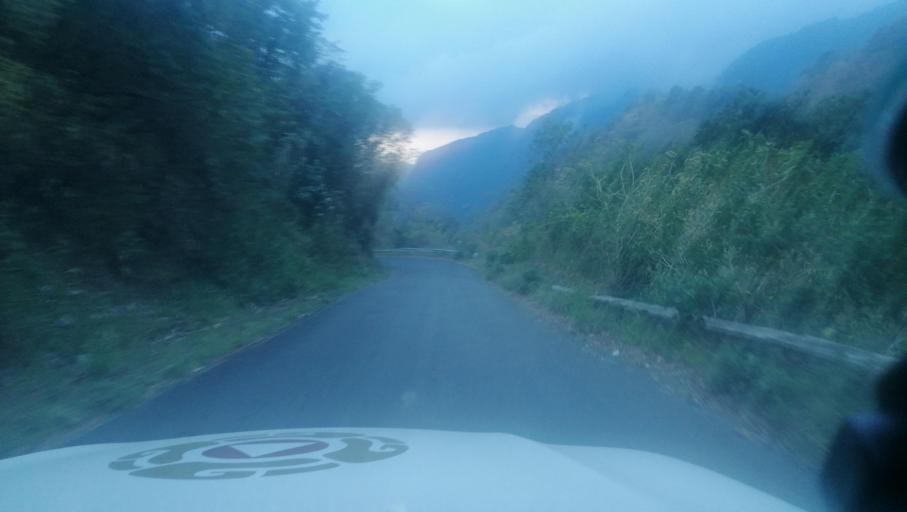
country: MX
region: Chiapas
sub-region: Cacahoatan
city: Benito Juarez
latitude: 15.1416
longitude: -92.1952
